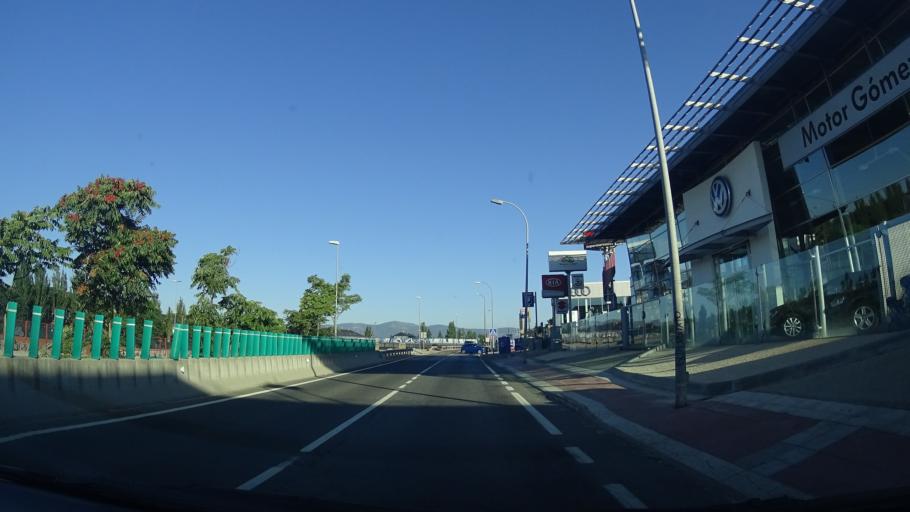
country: ES
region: Madrid
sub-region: Provincia de Madrid
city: Collado-Villalba
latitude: 40.6297
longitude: -3.9972
